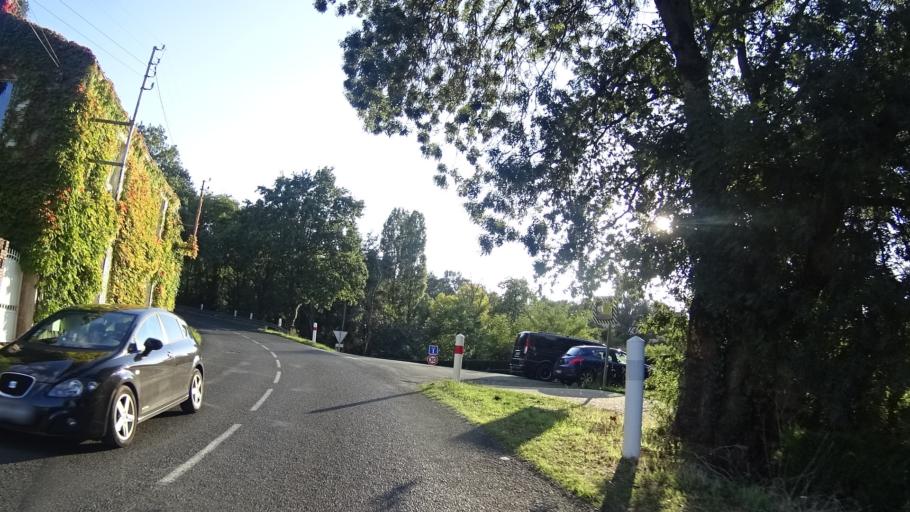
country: FR
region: Pays de la Loire
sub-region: Departement de Maine-et-Loire
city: Champtoceaux
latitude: 47.3389
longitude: -1.2558
